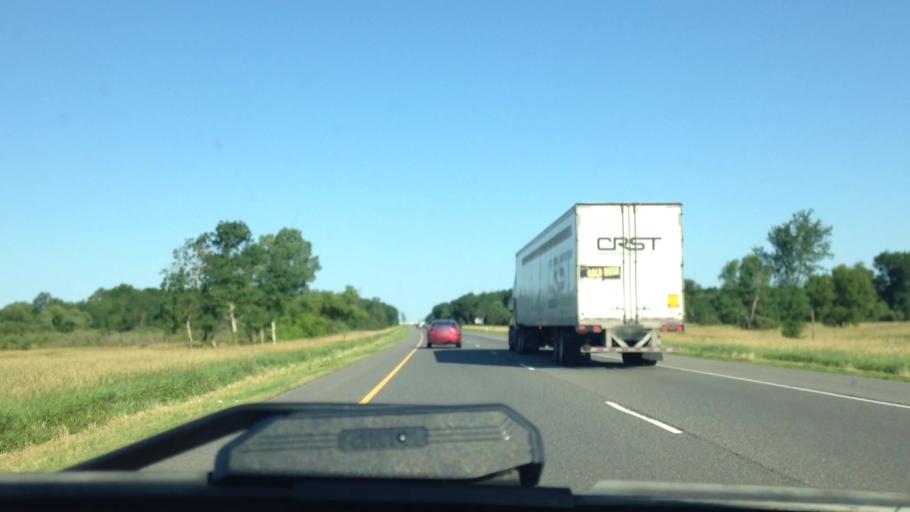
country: US
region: Wisconsin
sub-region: Monroe County
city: Tomah
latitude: 43.9497
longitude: -90.3301
